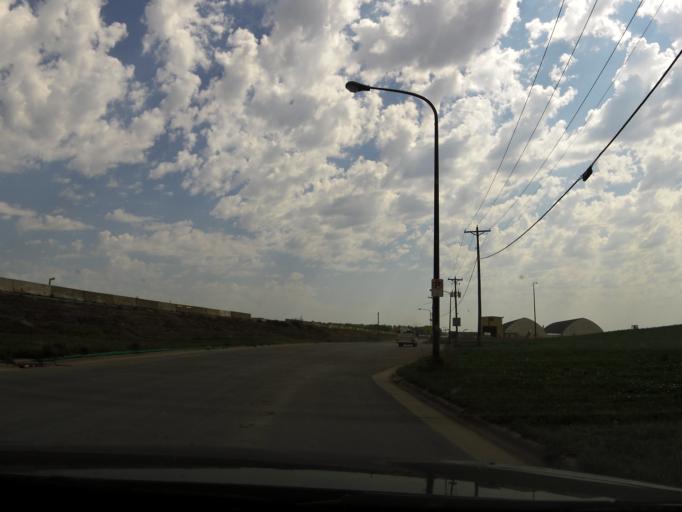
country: US
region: Minnesota
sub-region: Ramsey County
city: Saint Paul
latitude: 44.9421
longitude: -93.0517
